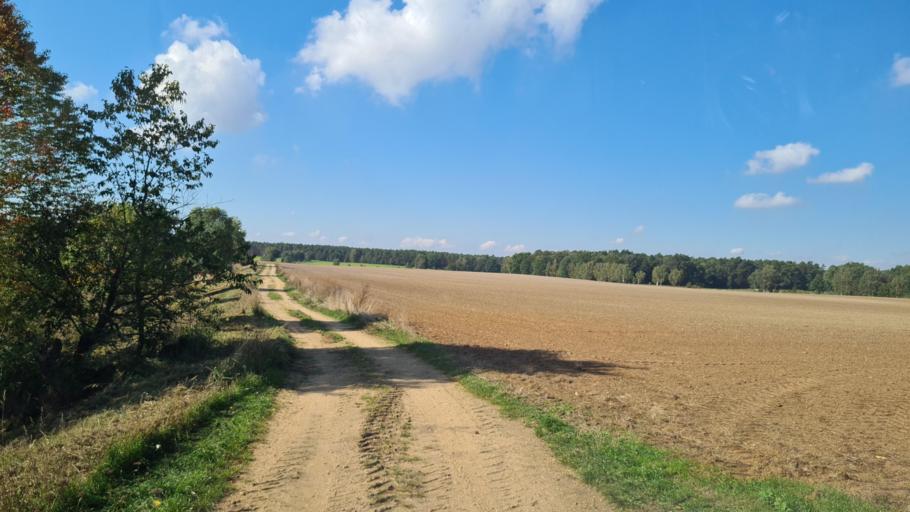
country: DE
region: Brandenburg
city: Lebusa
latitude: 51.8221
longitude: 13.4585
